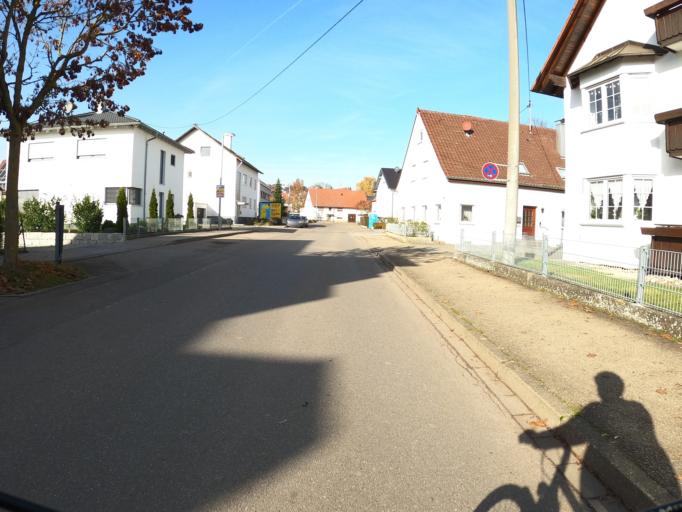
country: DE
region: Bavaria
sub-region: Swabia
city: Nersingen
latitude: 48.4568
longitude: 10.1053
